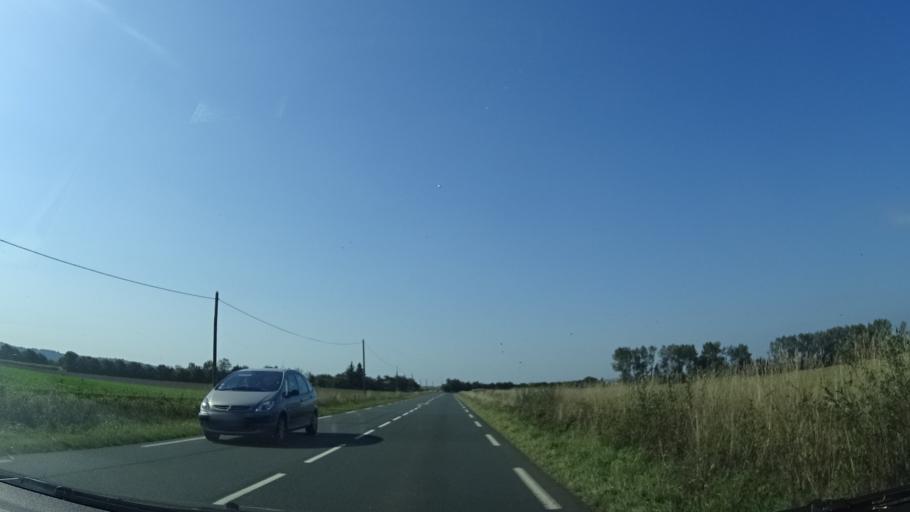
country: FR
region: Brittany
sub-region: Departement du Finistere
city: Plonevez-Porzay
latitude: 48.1348
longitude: -4.1868
